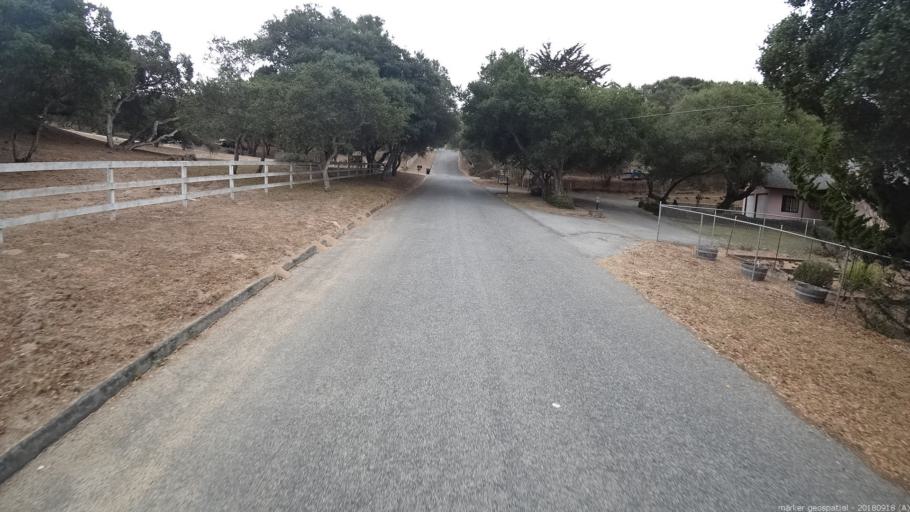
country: US
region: California
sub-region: Monterey County
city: Prunedale
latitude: 36.7803
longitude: -121.6335
